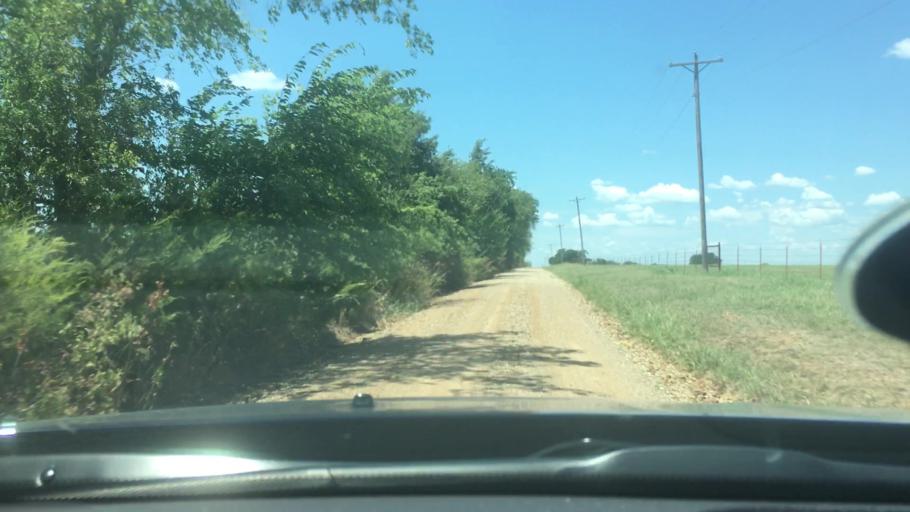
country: US
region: Oklahoma
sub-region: Bryan County
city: Durant
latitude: 33.9973
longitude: -96.1055
